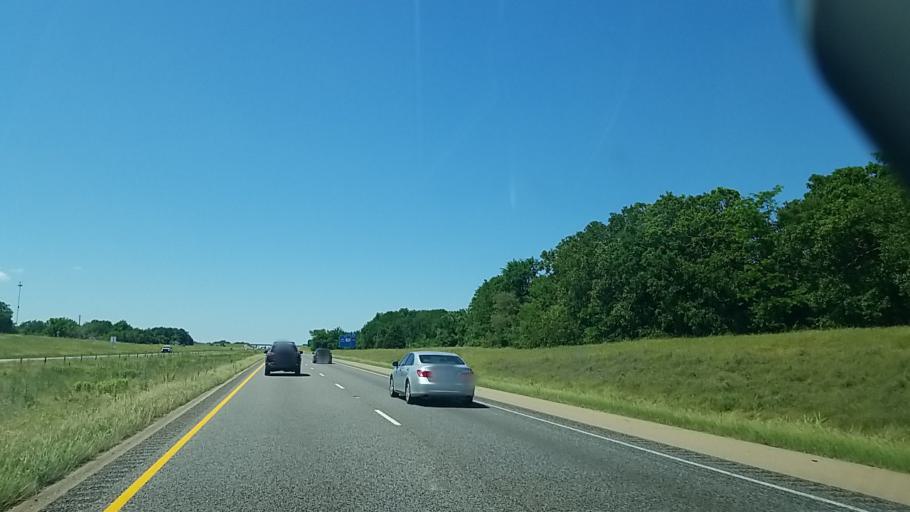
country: US
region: Texas
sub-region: Freestone County
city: Fairfield
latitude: 31.5873
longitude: -96.1506
